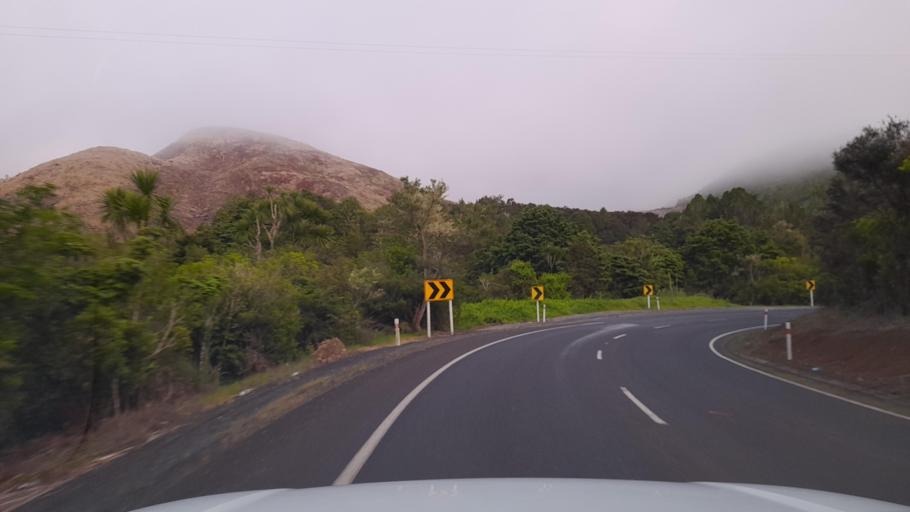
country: NZ
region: Northland
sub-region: Far North District
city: Moerewa
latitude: -35.6173
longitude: 173.8437
